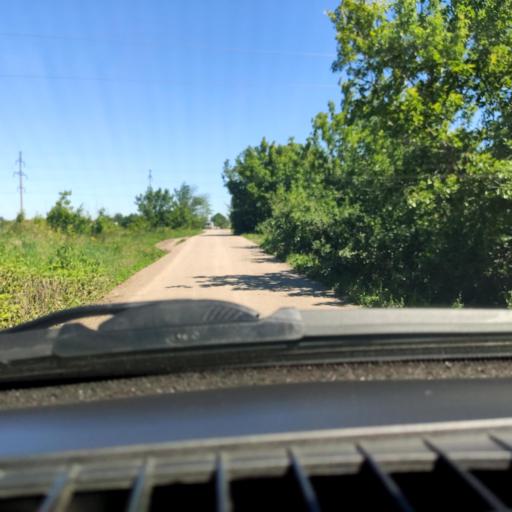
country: RU
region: Samara
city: Tol'yatti
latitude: 53.5868
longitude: 49.4328
